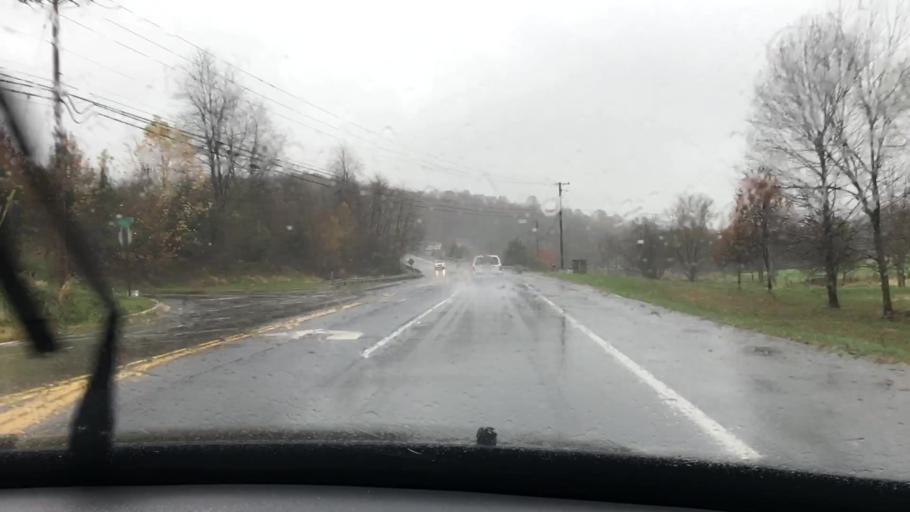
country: US
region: Maryland
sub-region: Carroll County
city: Westminster
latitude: 39.5630
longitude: -77.0060
